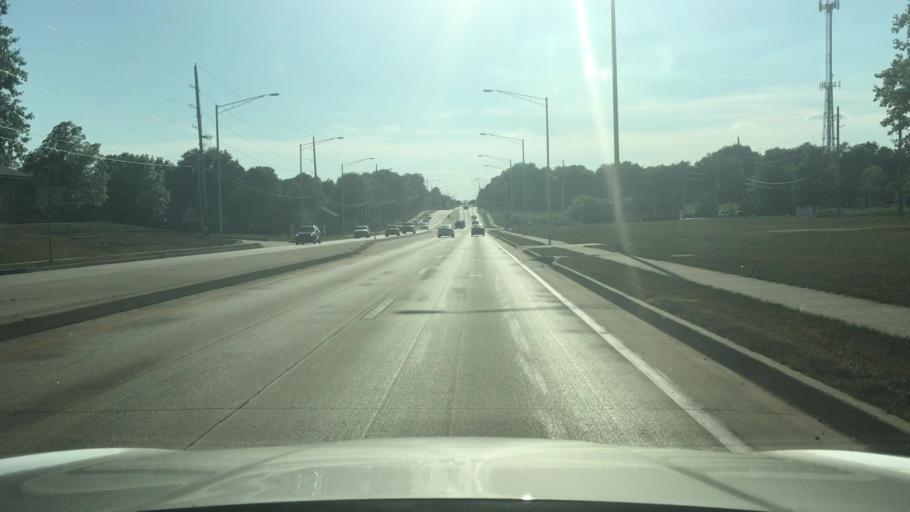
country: US
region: Missouri
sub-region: Cass County
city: Lake Winnebago
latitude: 38.8530
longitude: -94.3852
